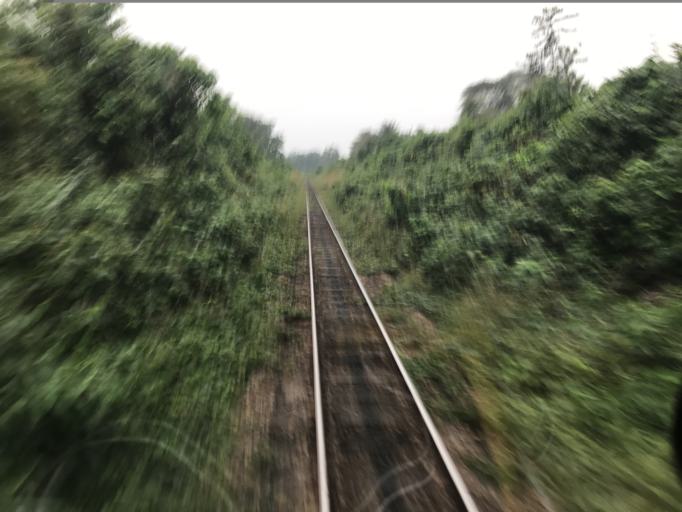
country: CM
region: Littoral
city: Edea
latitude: 3.9496
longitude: 10.0882
